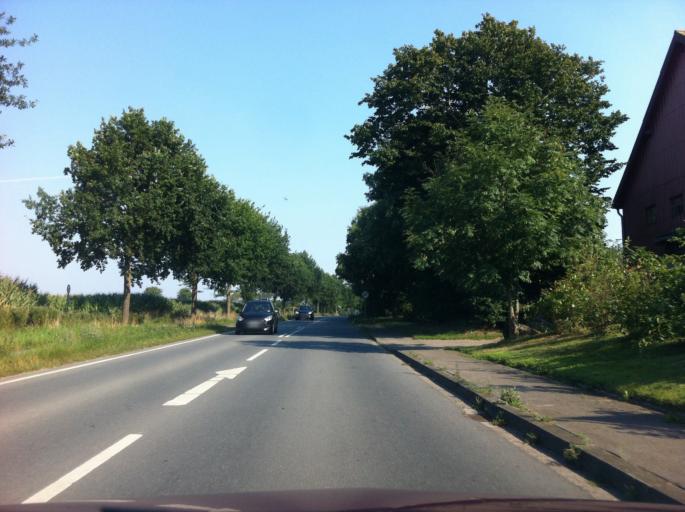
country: DE
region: Schleswig-Holstein
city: Harmsdorf
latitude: 54.3050
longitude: 10.8326
